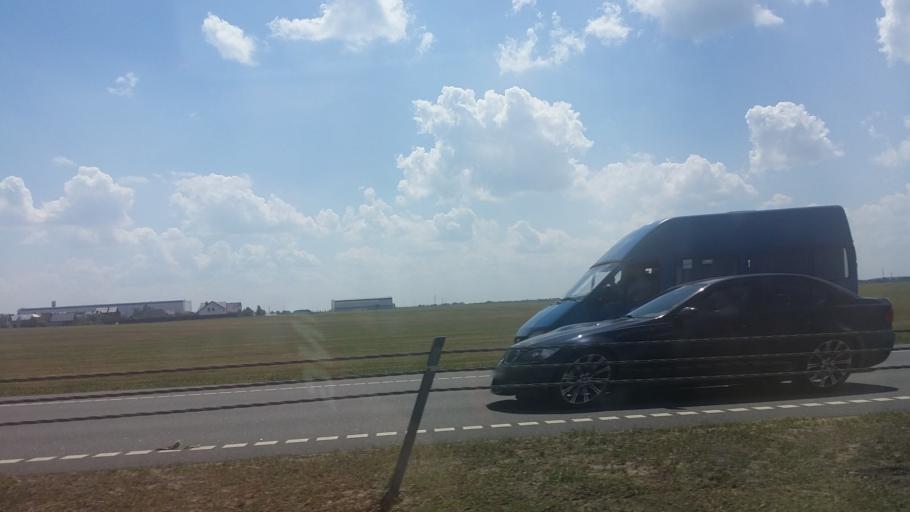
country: BY
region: Minsk
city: Luhavaya Slabada
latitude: 53.7615
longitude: 27.9053
